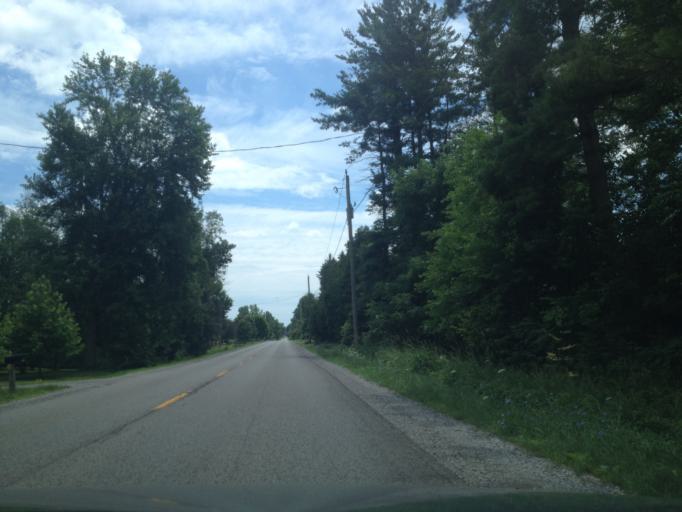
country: CA
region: Ontario
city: Norfolk County
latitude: 42.8044
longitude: -80.3160
